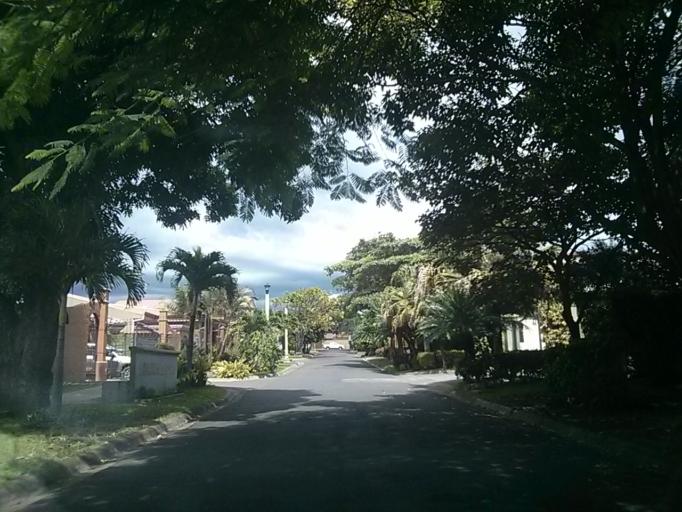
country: CR
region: Heredia
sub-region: Canton de Belen
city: San Antonio
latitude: 9.9642
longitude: -84.1938
